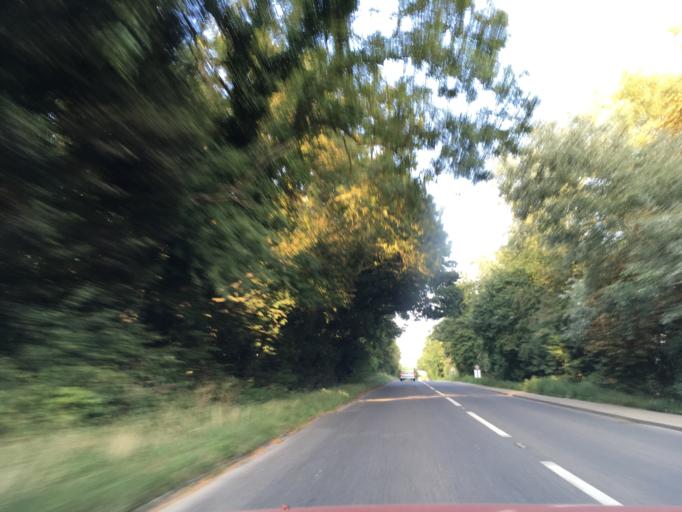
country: GB
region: England
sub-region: Gloucestershire
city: Bourton on the Water
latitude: 51.8893
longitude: -1.7656
